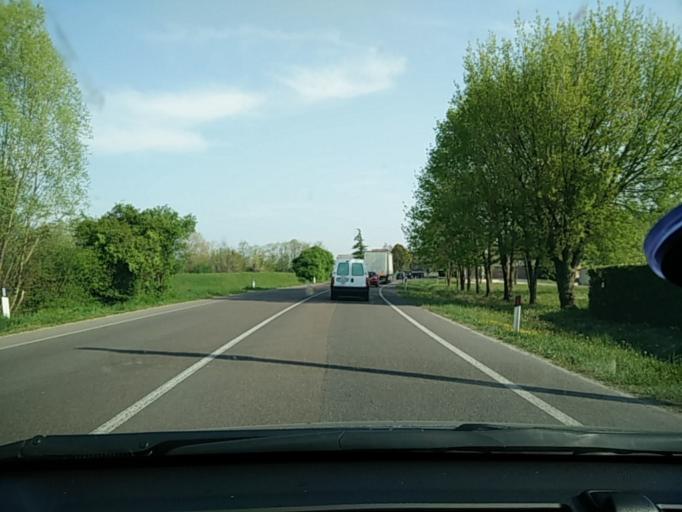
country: IT
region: Veneto
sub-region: Provincia di Treviso
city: Portobuffole
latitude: 45.8541
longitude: 12.5358
